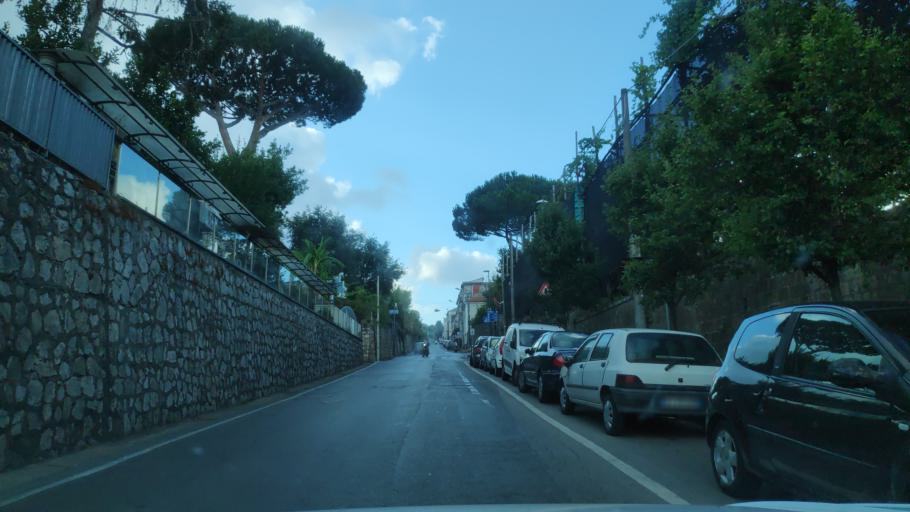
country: IT
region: Campania
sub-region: Provincia di Napoli
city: Piano di Sorrento
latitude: 40.6340
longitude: 14.4175
